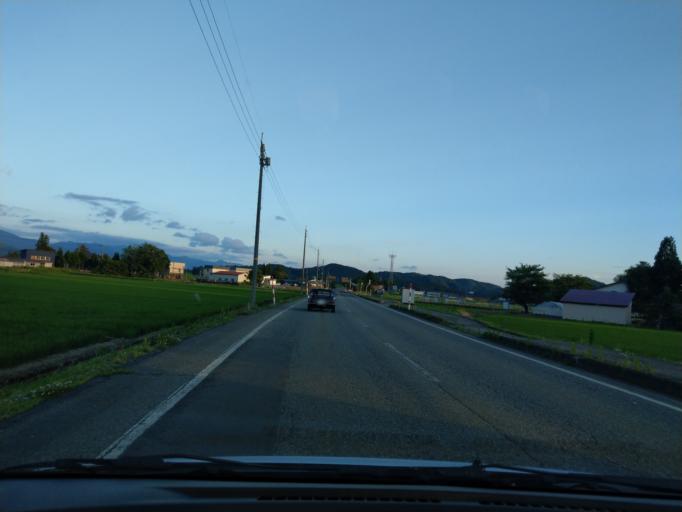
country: JP
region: Akita
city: Kakunodatemachi
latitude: 39.6255
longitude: 140.5715
